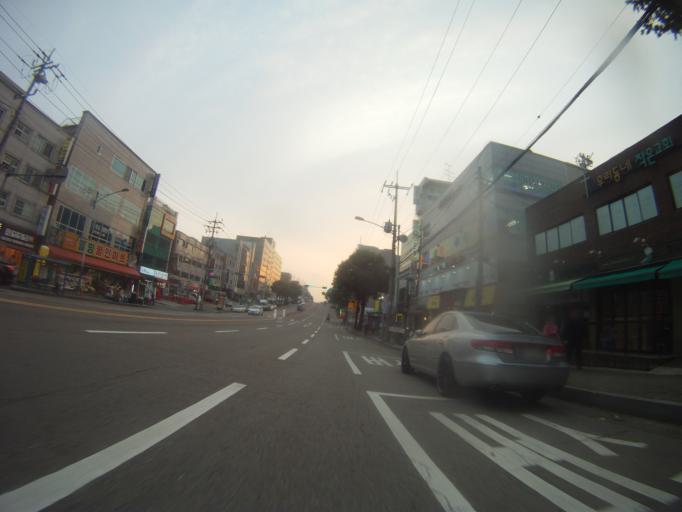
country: KR
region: Incheon
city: Incheon
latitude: 37.4581
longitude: 126.6888
